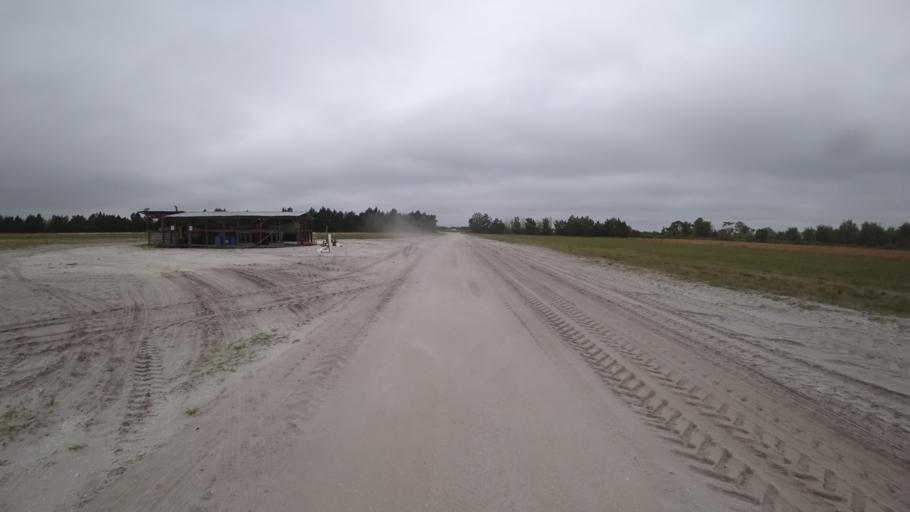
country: US
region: Florida
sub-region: Sarasota County
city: Warm Mineral Springs
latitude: 27.3012
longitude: -82.1454
